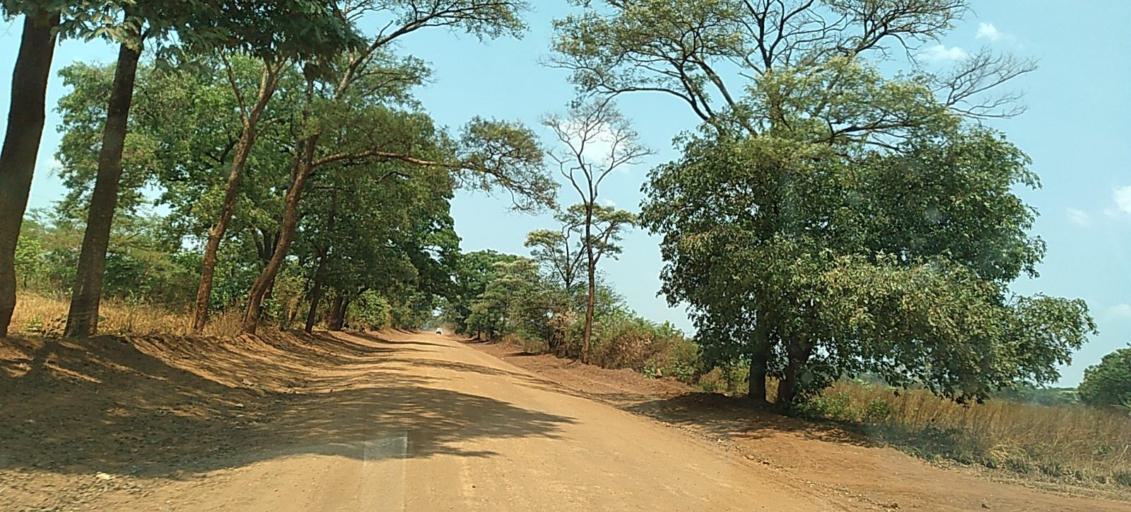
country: ZM
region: Copperbelt
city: Mpongwe
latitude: -13.5151
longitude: 28.0144
